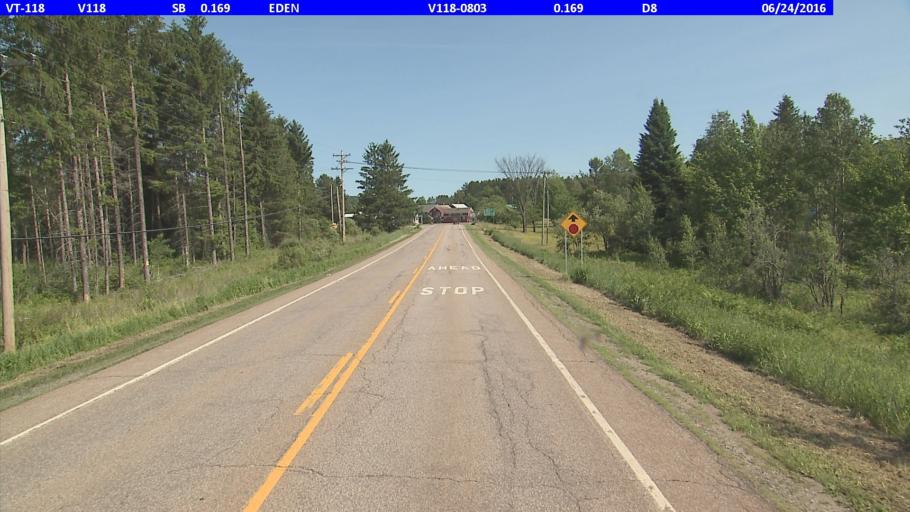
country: US
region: Vermont
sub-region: Lamoille County
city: Hyde Park
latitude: 44.7092
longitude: -72.5477
